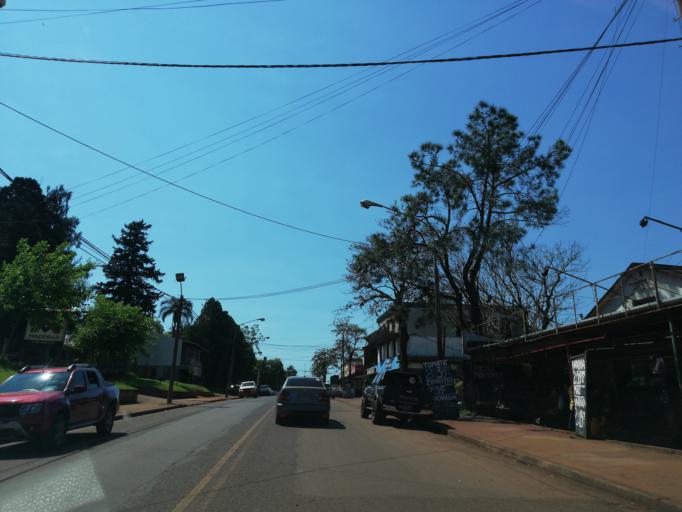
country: AR
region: Misiones
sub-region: Departamento de Eldorado
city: Eldorado
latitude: -26.4039
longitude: -54.6267
